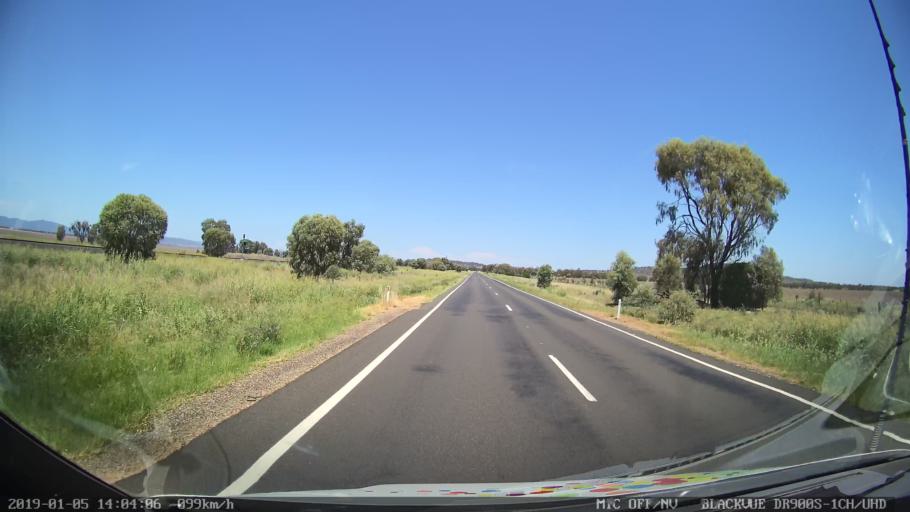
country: AU
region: New South Wales
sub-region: Gunnedah
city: Gunnedah
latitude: -31.1966
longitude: 150.3596
